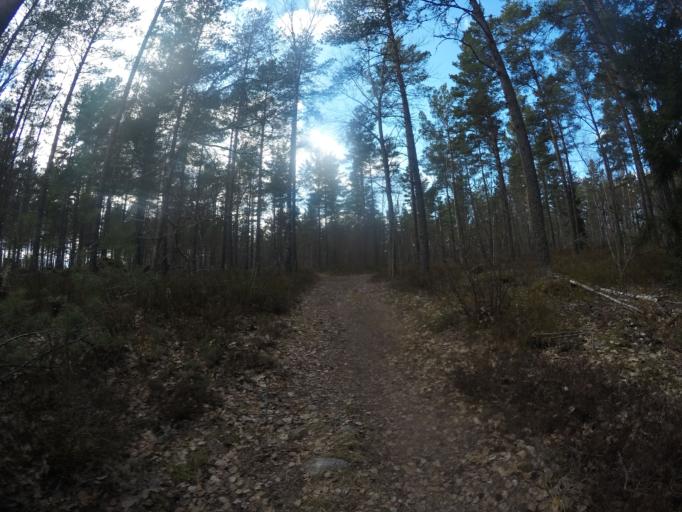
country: SE
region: Soedermanland
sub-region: Eskilstuna Kommun
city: Hallbybrunn
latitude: 59.3878
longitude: 16.4045
